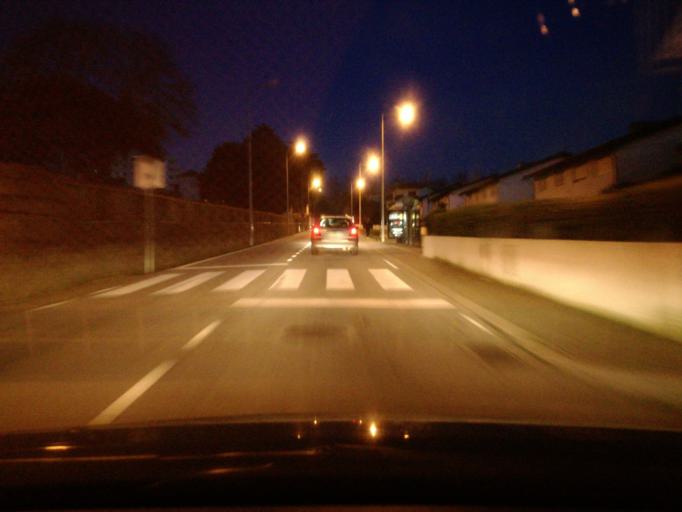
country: PT
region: Porto
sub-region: Maia
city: Maia
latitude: 41.2379
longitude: -8.6309
